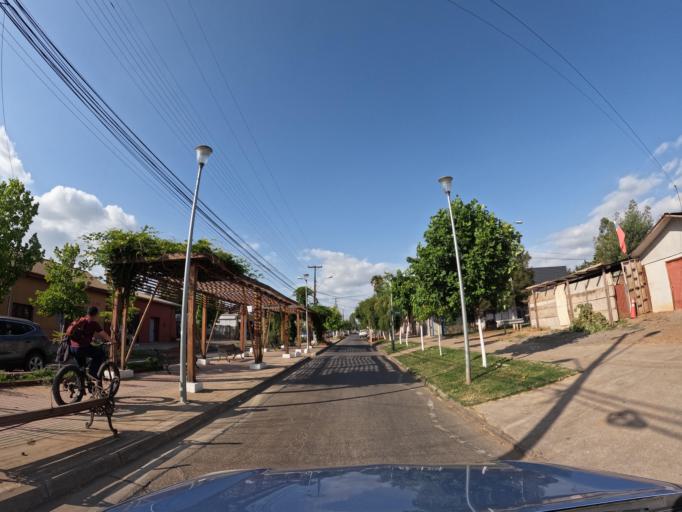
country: CL
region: Maule
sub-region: Provincia de Curico
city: Molina
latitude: -35.2843
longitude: -71.2608
